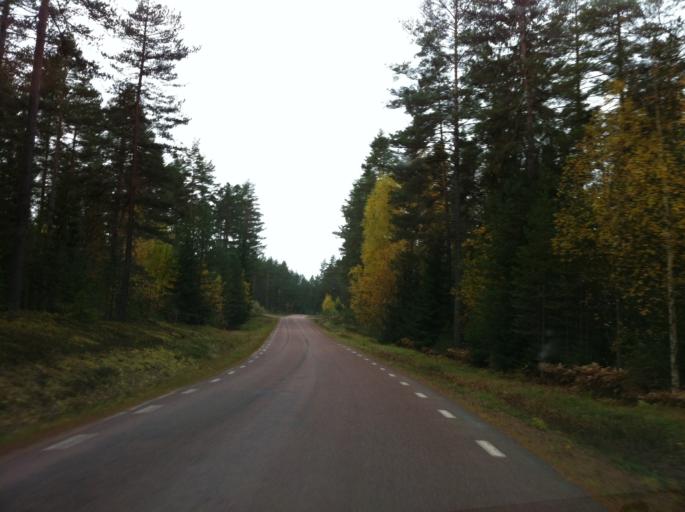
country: SE
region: Dalarna
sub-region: Mora Kommun
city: Mora
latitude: 61.0862
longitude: 14.3909
